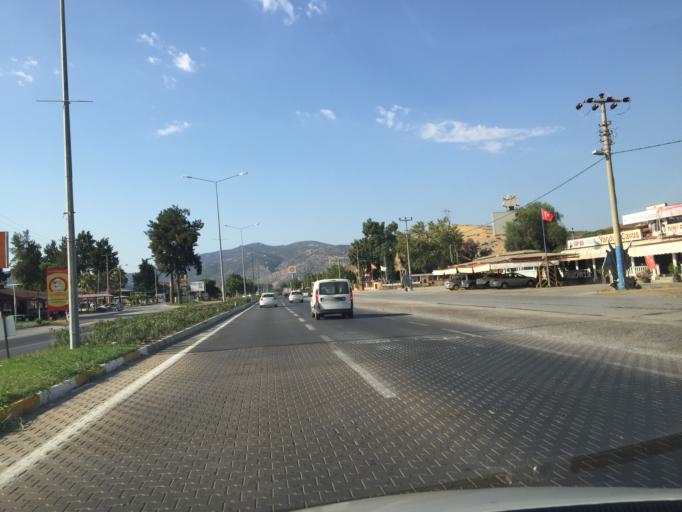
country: TR
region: Izmir
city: Selcuk
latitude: 37.9617
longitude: 27.3727
